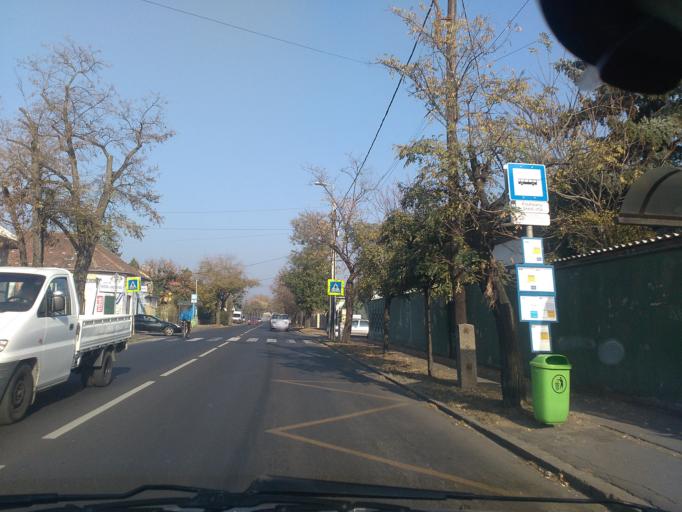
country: HU
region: Budapest
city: Budapest XVIII. keruelet
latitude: 47.4491
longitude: 19.1929
